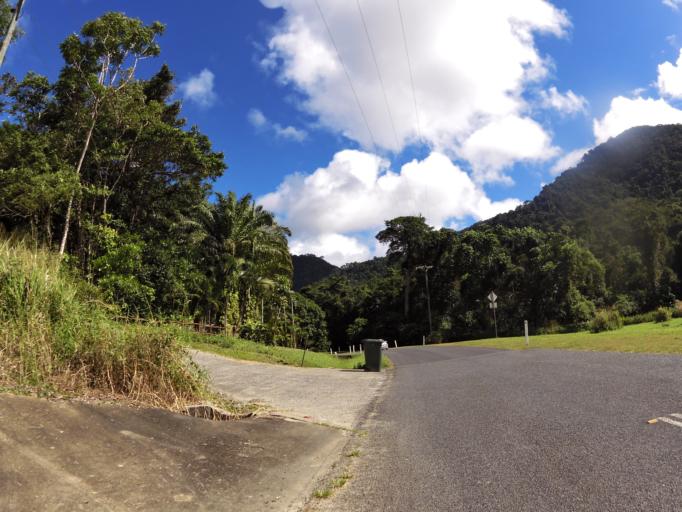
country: AU
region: Queensland
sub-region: Cairns
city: Woree
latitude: -16.9578
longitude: 145.6845
